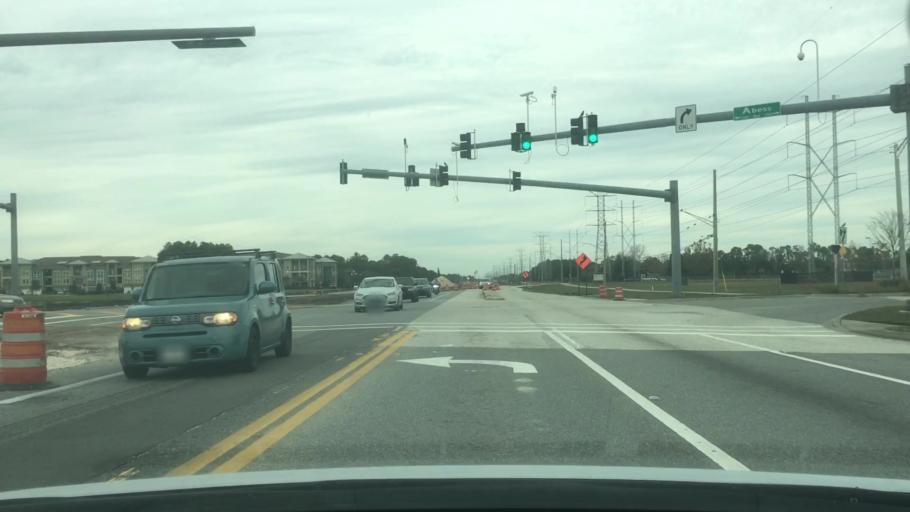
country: US
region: Florida
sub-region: Duval County
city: Atlantic Beach
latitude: 30.3219
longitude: -81.4894
